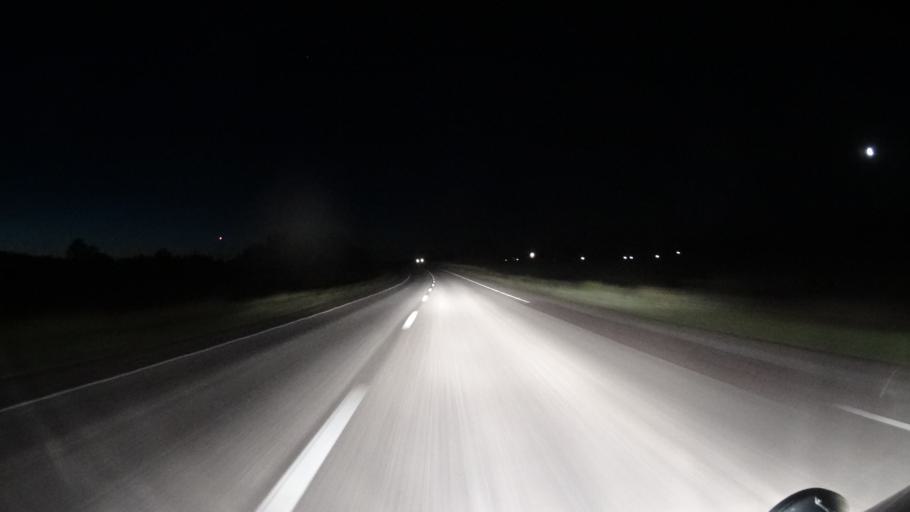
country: SE
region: OEstergoetland
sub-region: Odeshogs Kommun
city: OEdeshoeg
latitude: 58.2601
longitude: 14.7422
